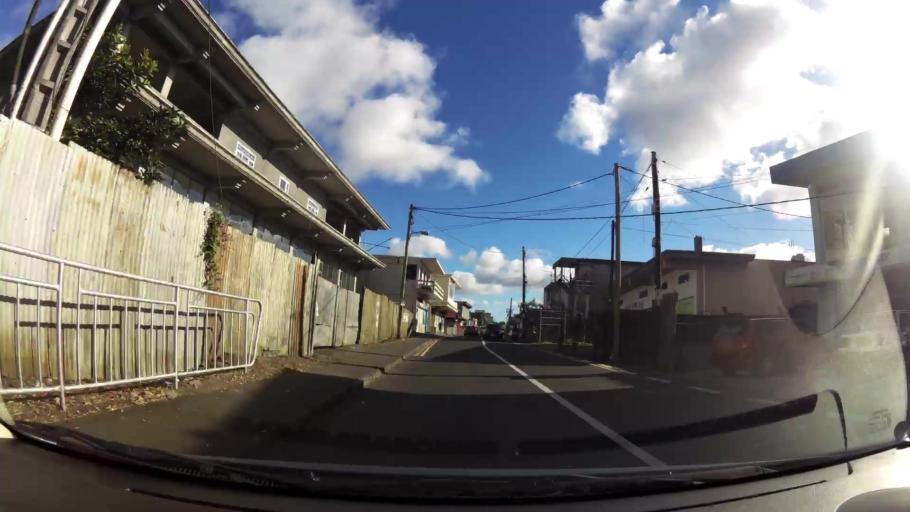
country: MU
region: Plaines Wilhems
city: Curepipe
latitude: -20.2935
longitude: 57.5188
